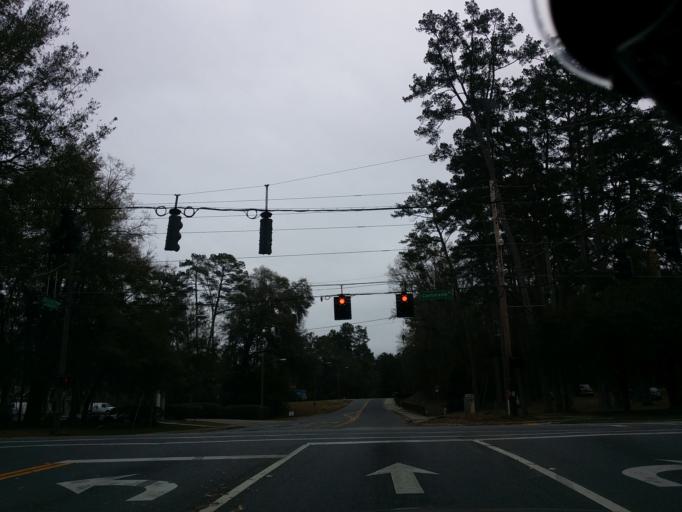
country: US
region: Florida
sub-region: Leon County
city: Tallahassee
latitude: 30.4858
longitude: -84.2291
